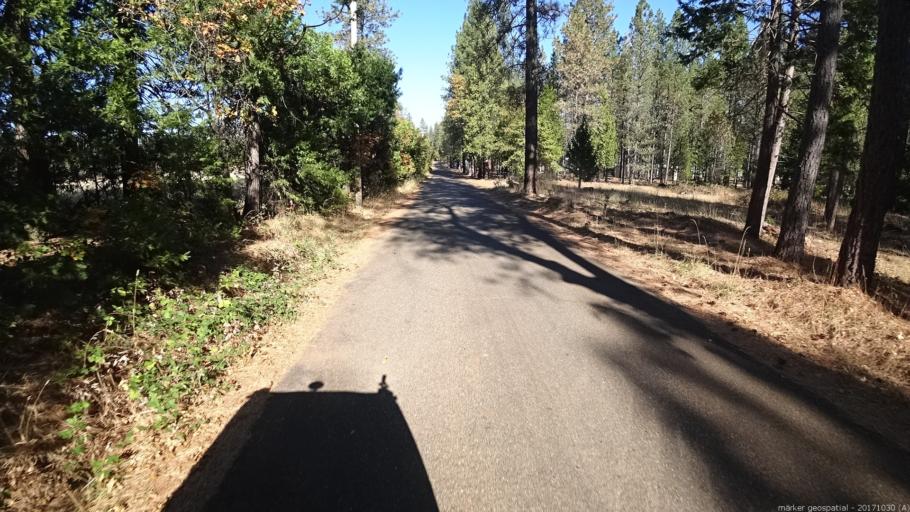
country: US
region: California
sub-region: Shasta County
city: Shingletown
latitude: 40.6294
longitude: -121.8949
